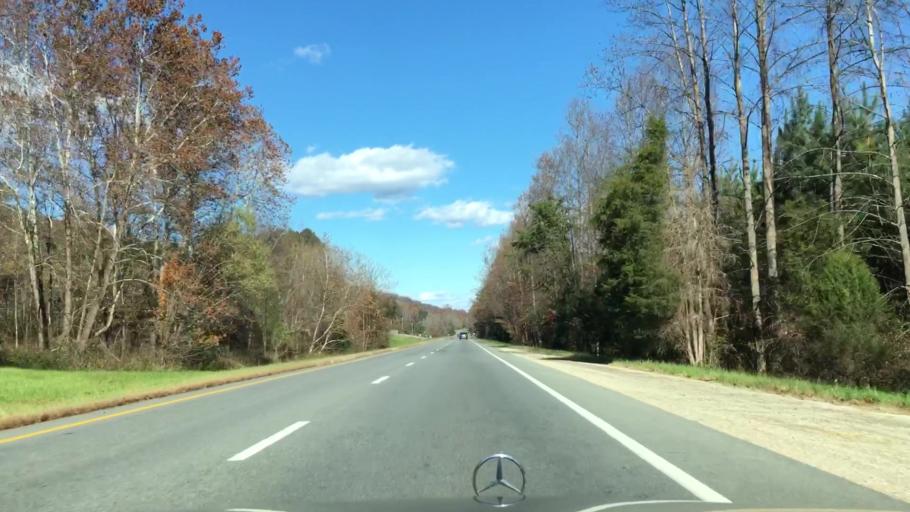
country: US
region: Virginia
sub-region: Albemarle County
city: Crozet
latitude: 37.9124
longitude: -78.6877
